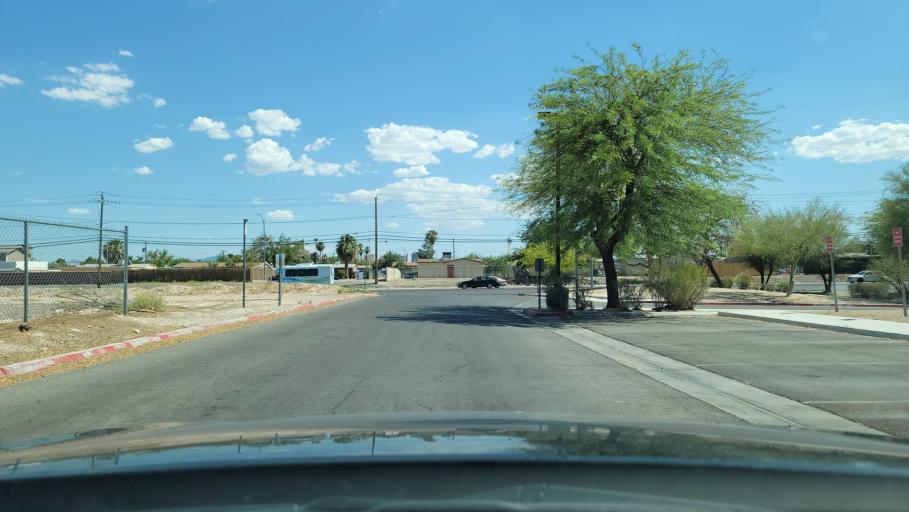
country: US
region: Nevada
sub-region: Clark County
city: Las Vegas
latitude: 36.1964
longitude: -115.1495
